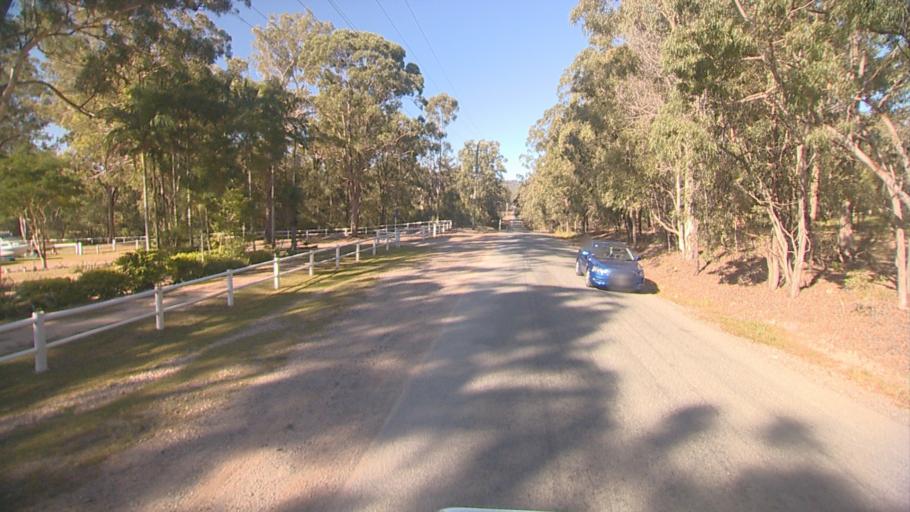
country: AU
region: Queensland
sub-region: Logan
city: Chambers Flat
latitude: -27.7620
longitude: 153.1287
